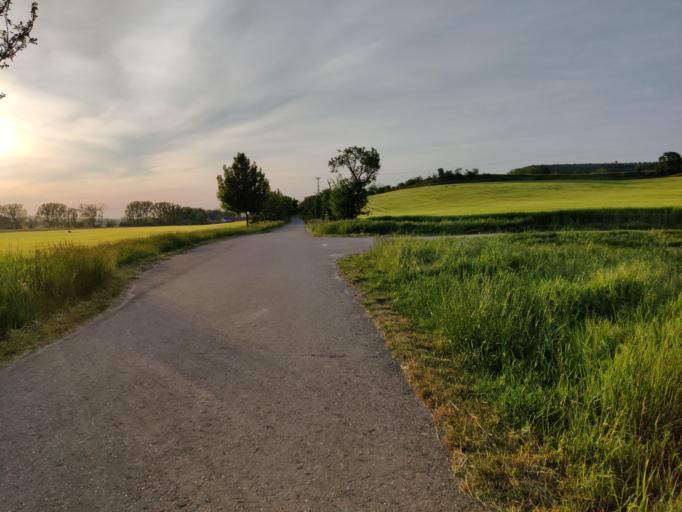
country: DE
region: Saxony-Anhalt
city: Balgstadt
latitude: 51.2156
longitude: 11.7110
